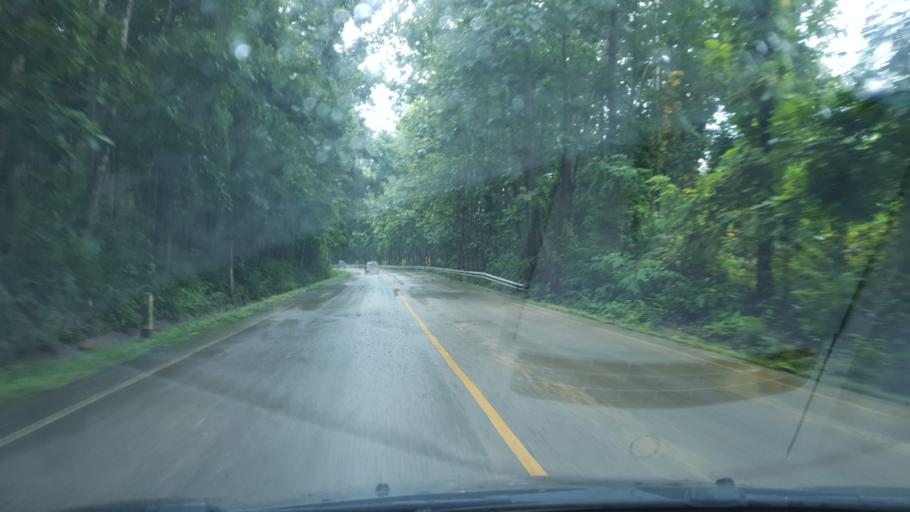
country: TH
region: Mae Hong Son
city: Pa Pae
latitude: 18.2474
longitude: 97.9428
